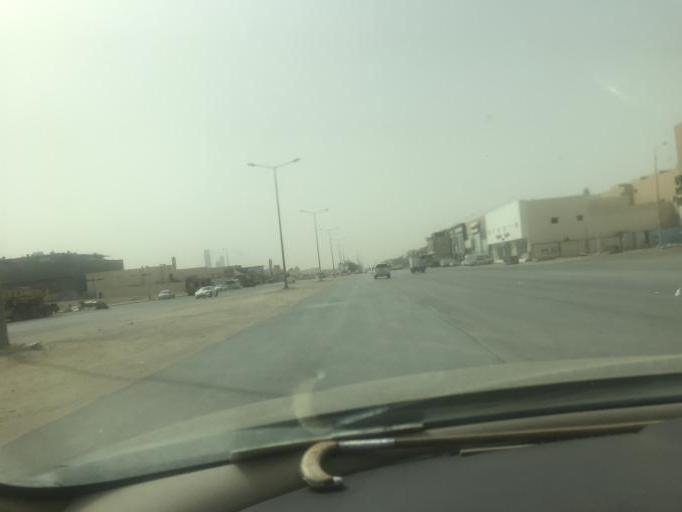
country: SA
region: Ar Riyad
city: Riyadh
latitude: 24.8049
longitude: 46.6032
